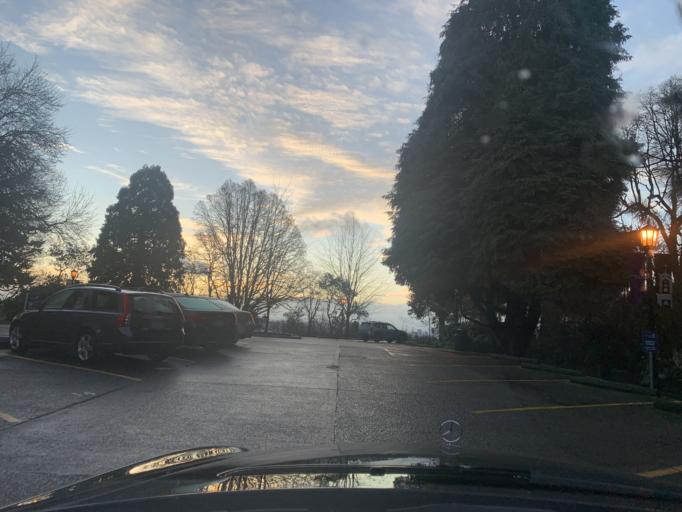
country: US
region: Oregon
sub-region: Multnomah County
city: Portland
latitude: 45.5716
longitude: -122.7251
